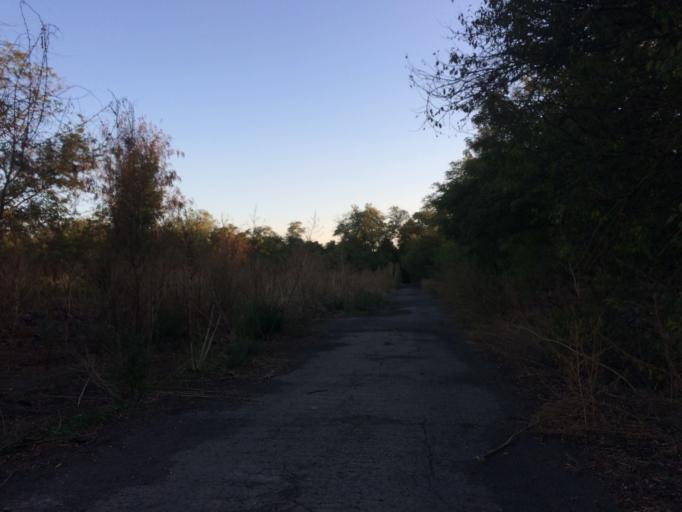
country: RU
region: Rostov
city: Gigant
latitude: 46.5112
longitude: 41.1942
